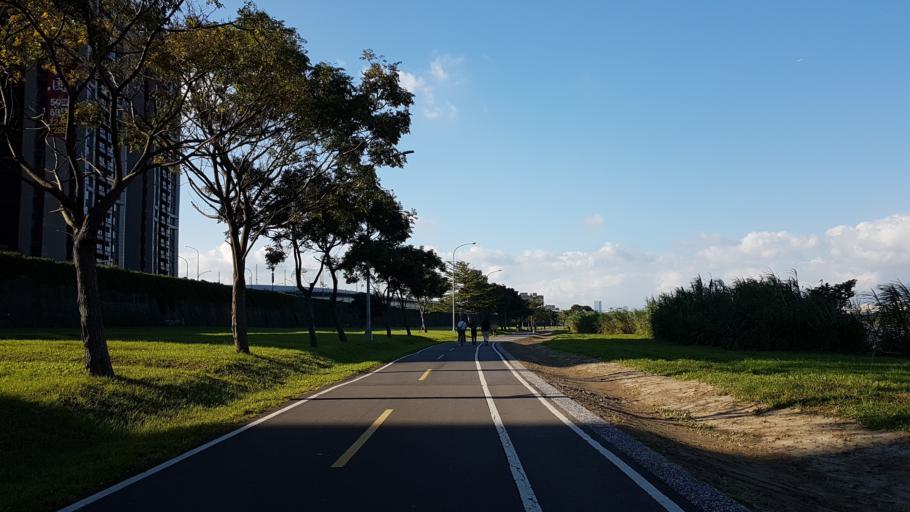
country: TW
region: Taipei
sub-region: Taipei
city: Banqiao
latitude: 25.0120
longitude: 121.4891
